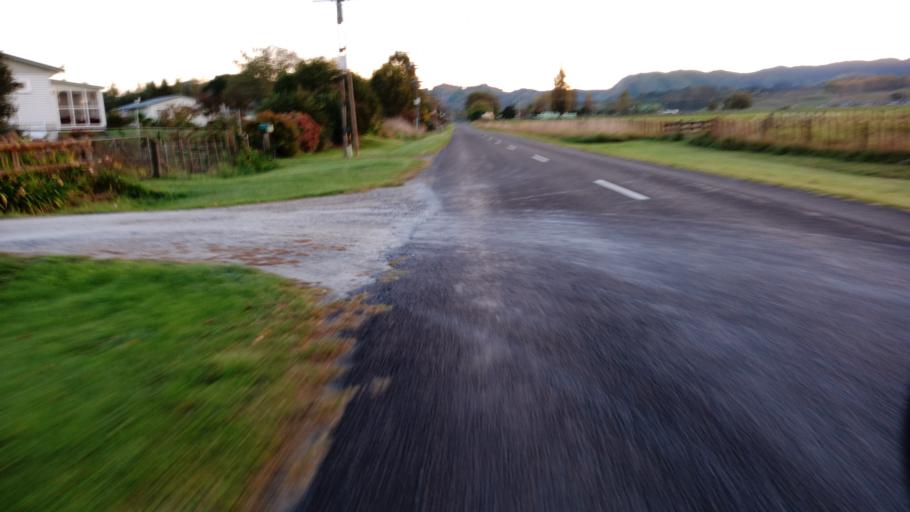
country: NZ
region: Gisborne
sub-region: Gisborne District
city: Gisborne
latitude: -38.6411
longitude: 177.9828
